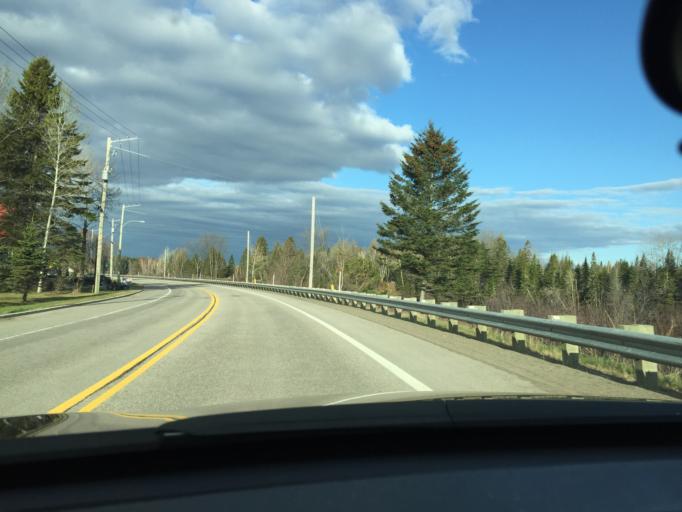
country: CA
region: Quebec
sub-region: Capitale-Nationale
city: Shannon
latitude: 46.8662
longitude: -71.5365
